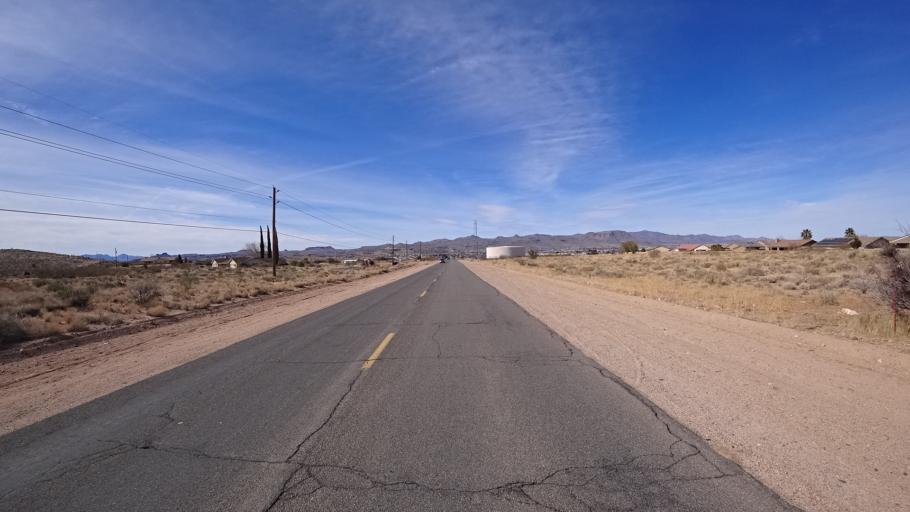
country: US
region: Arizona
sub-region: Mohave County
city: Kingman
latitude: 35.1833
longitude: -114.0011
